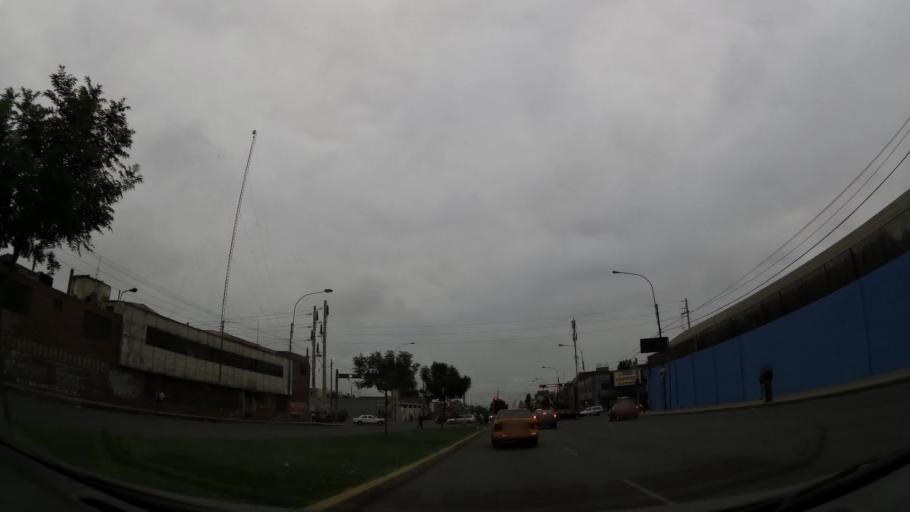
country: PE
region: Lima
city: Lima
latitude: -12.0568
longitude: -77.0633
